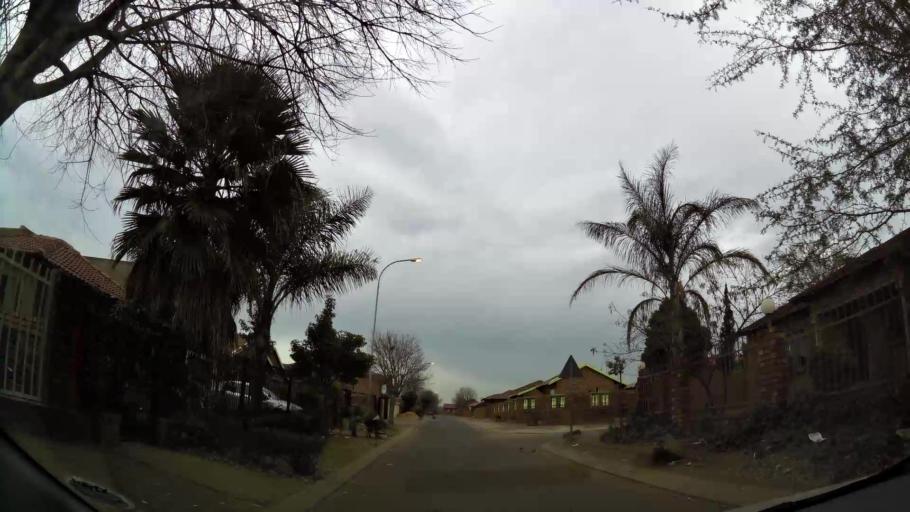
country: ZA
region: Gauteng
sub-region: City of Tshwane Metropolitan Municipality
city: Pretoria
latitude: -25.7203
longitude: 28.3518
